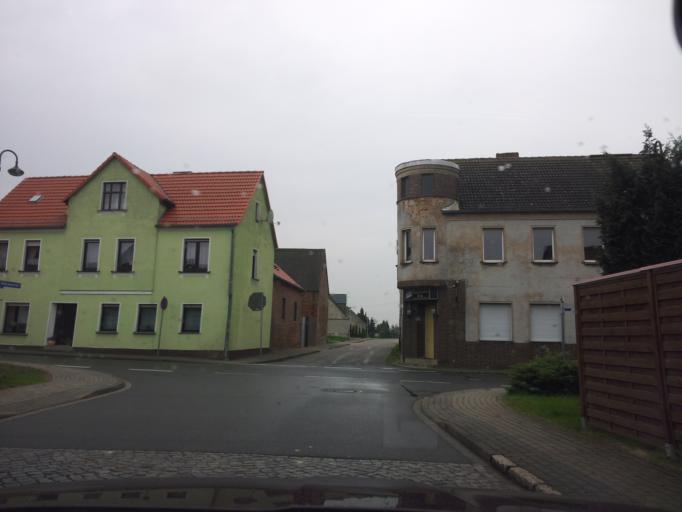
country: DE
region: Brandenburg
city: Niedergorsdorf
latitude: 52.0083
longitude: 12.9377
